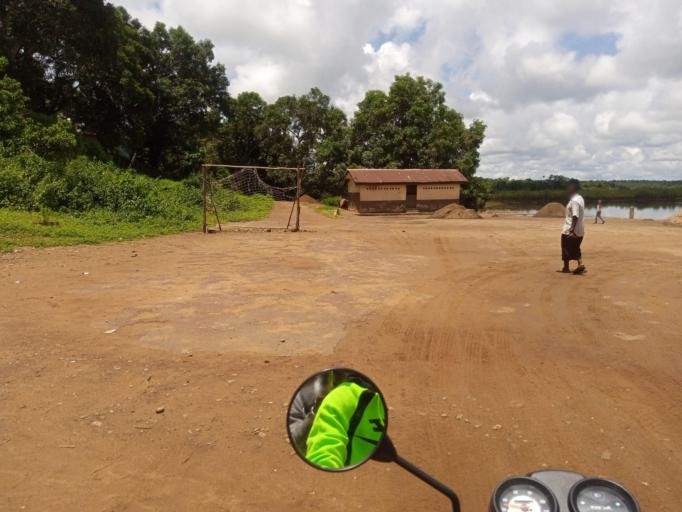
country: SL
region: Northern Province
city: Port Loko
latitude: 8.7631
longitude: -12.7920
